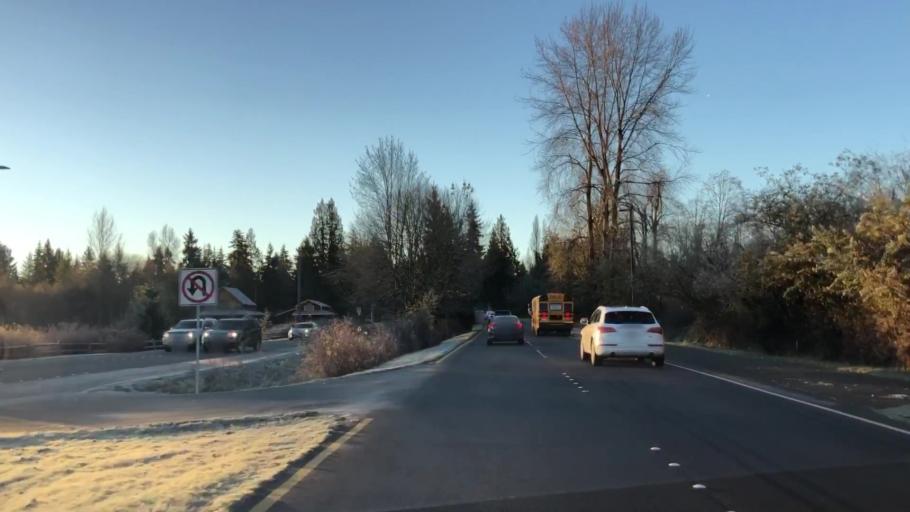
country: US
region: Washington
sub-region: King County
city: Eastgate
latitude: 47.6046
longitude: -122.1430
